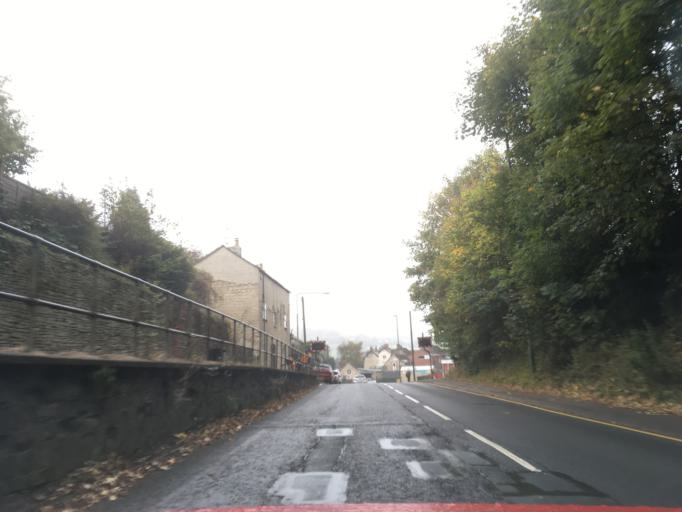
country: GB
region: England
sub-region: Gloucestershire
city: Stroud
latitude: 51.7464
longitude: -2.2386
